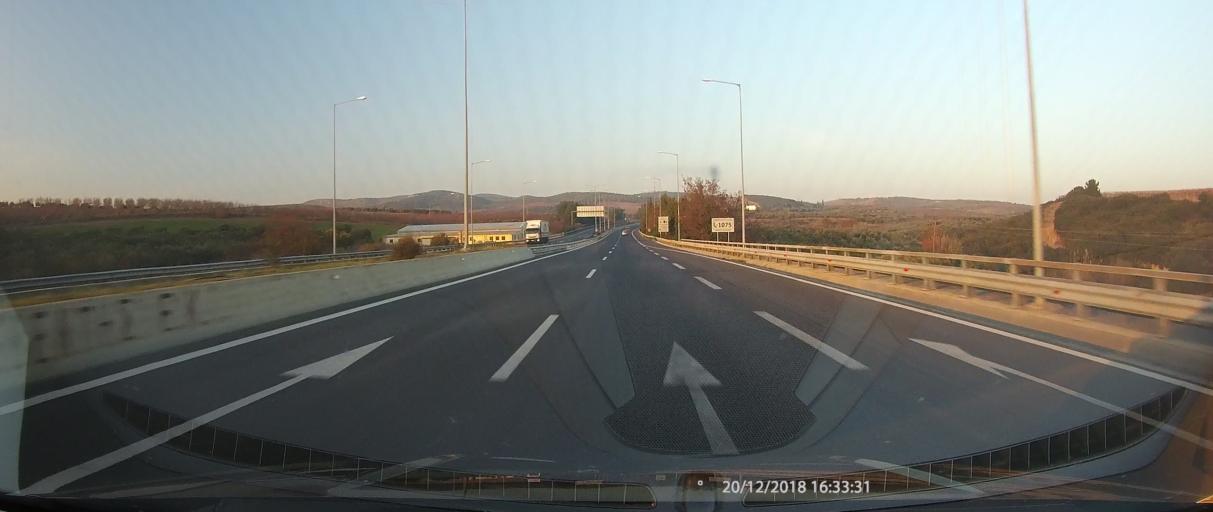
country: GR
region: Thessaly
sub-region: Nomos Magnisias
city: Evxinoupolis
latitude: 39.2658
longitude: 22.7376
